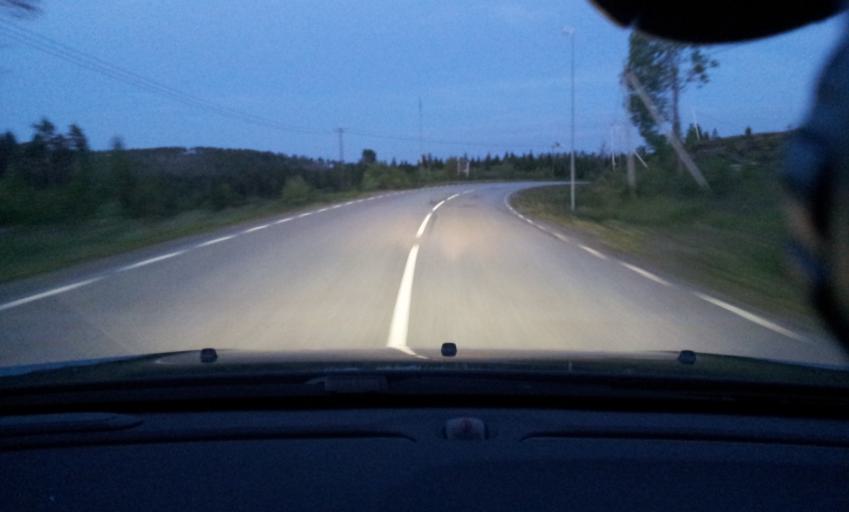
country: SE
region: Jaemtland
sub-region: OEstersunds Kommun
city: Brunflo
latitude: 62.6867
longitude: 14.9636
